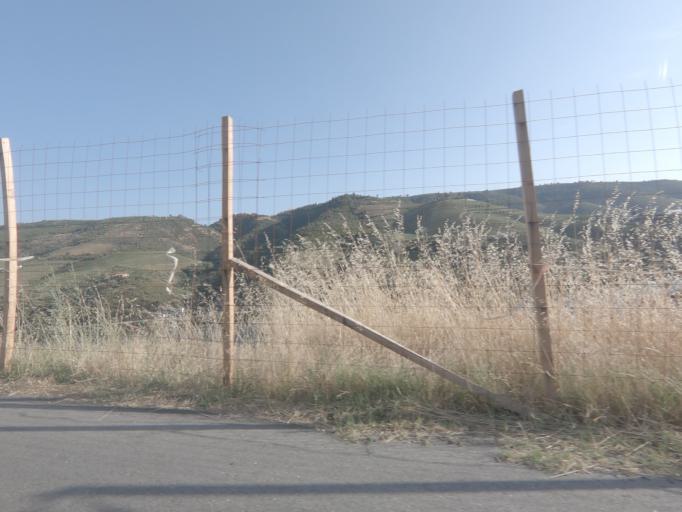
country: PT
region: Viseu
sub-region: Tabuaco
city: Tabuaco
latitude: 41.1620
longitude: -7.6079
